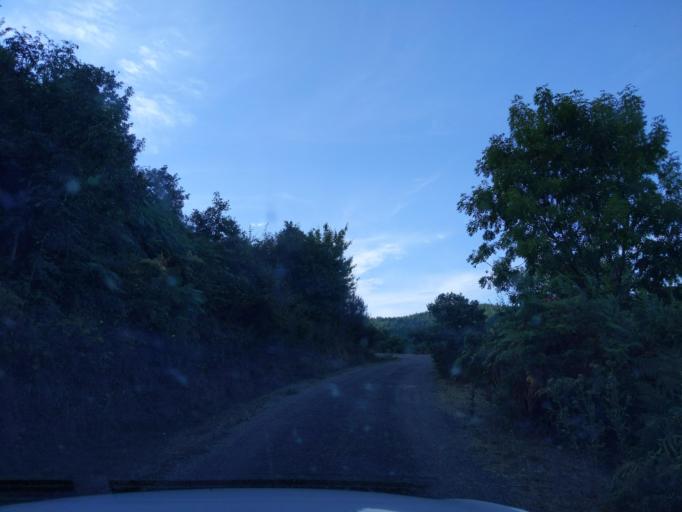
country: ES
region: La Rioja
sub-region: Provincia de La Rioja
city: Ojacastro
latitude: 42.3788
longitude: -3.0160
